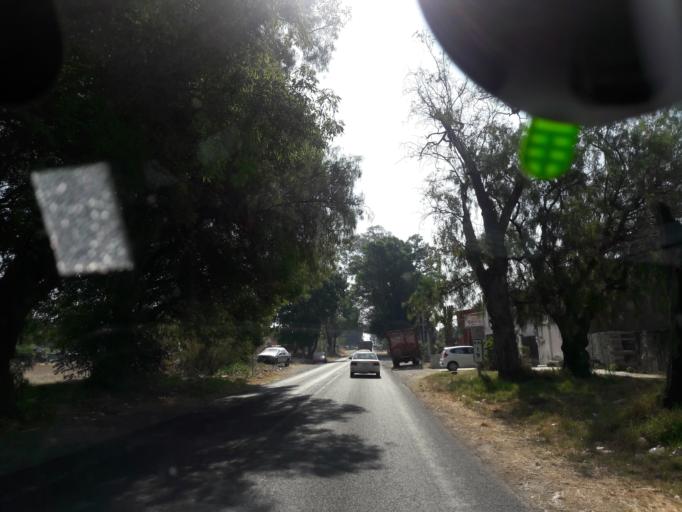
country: MX
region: Tlaxcala
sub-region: Panotla
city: Fraccionamiento la Virgen
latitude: 19.3196
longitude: -98.2773
